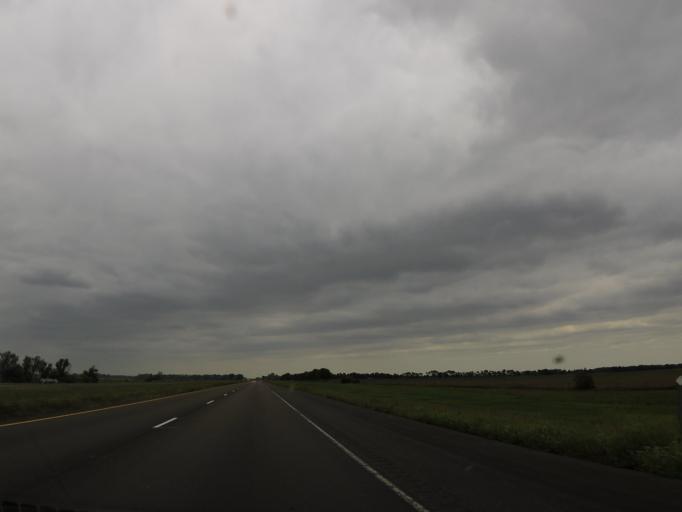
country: US
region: North Dakota
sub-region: Richland County
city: Wahpeton
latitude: 46.0198
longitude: -96.8354
